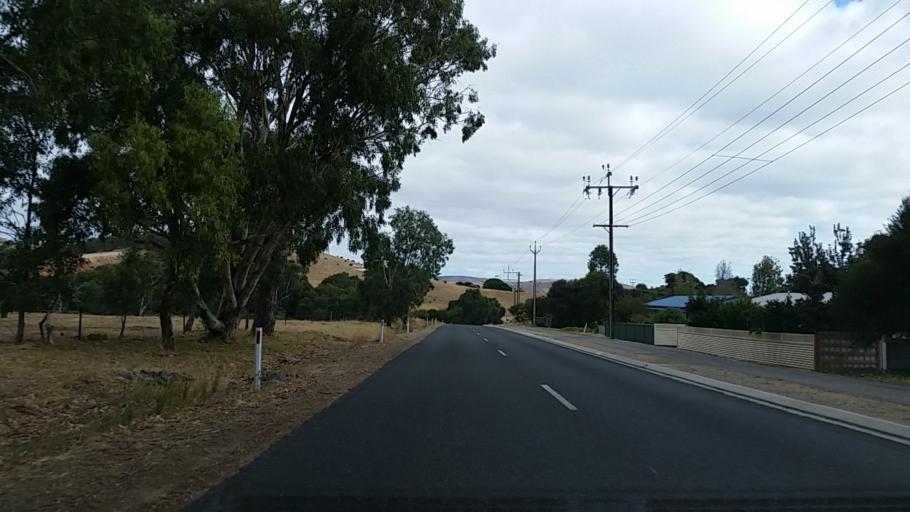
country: AU
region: South Australia
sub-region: Yankalilla
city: Normanville
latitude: -35.4300
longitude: 138.3258
